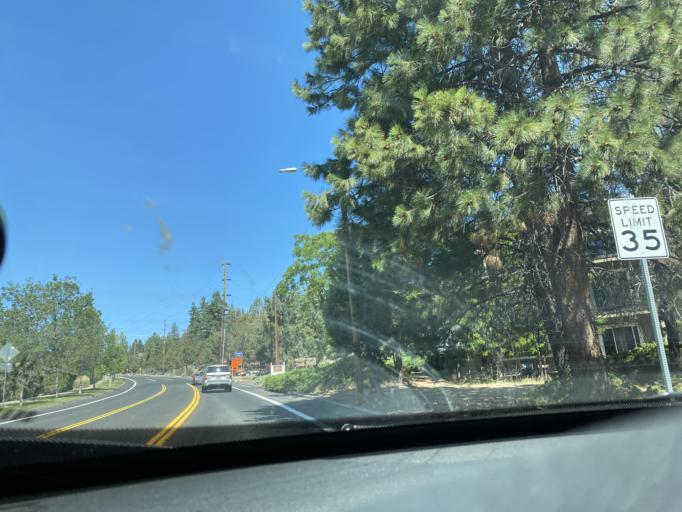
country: US
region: Oregon
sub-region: Deschutes County
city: Bend
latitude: 44.0635
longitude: -121.3385
